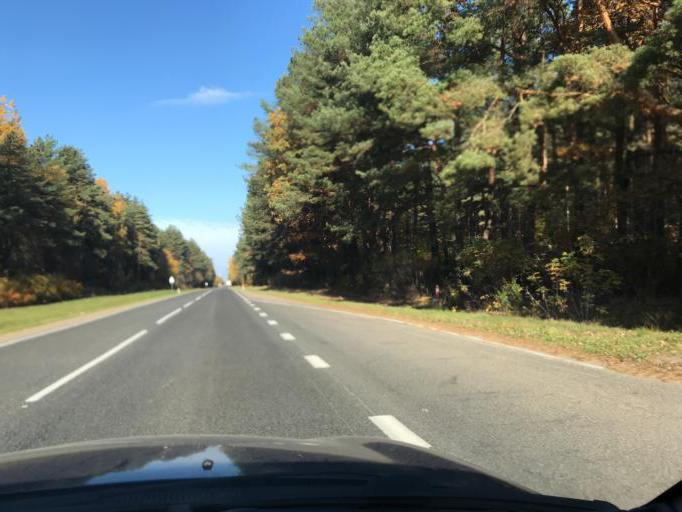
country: BY
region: Grodnenskaya
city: Lida
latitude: 53.9731
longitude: 25.2305
